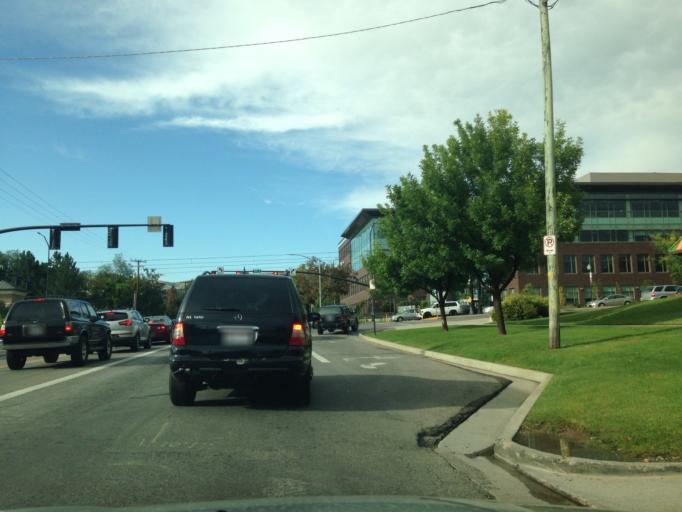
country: US
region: Utah
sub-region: Salt Lake County
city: Salt Lake City
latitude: 40.7601
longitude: -111.8653
